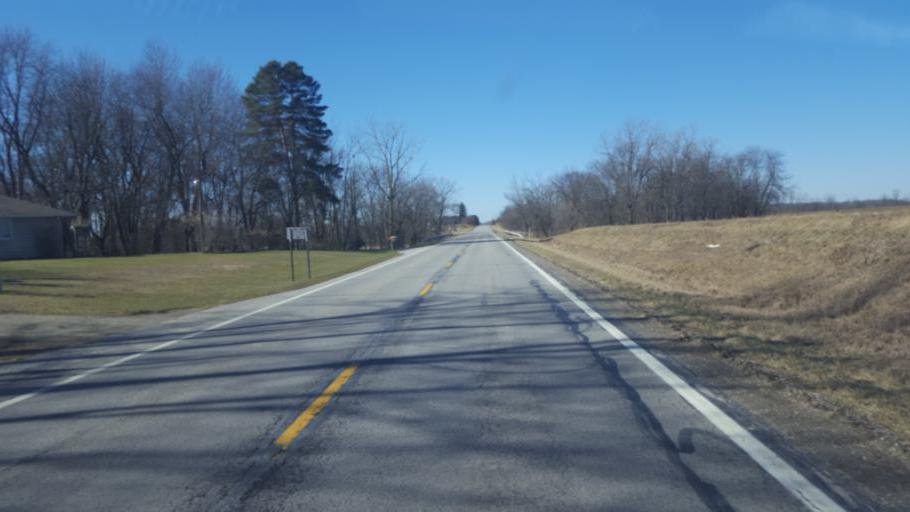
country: US
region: Ohio
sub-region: Wyandot County
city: Upper Sandusky
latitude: 40.6436
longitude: -83.3085
